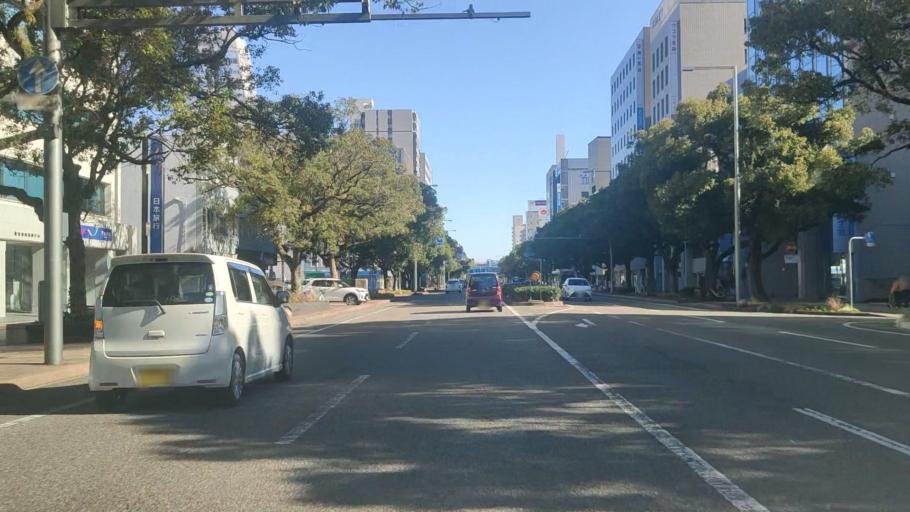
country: JP
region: Miyazaki
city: Miyazaki-shi
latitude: 31.9163
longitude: 131.4264
